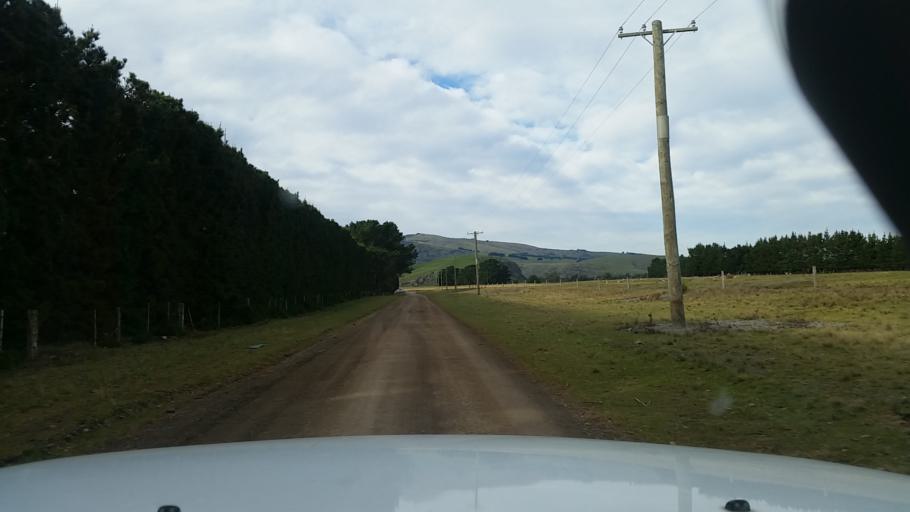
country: NZ
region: Canterbury
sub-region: Selwyn District
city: Lincoln
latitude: -43.8107
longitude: 172.6730
